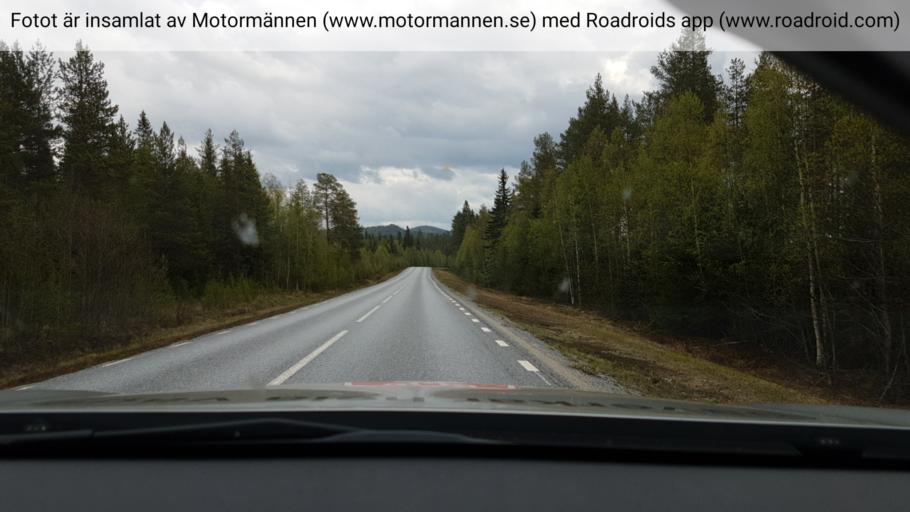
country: SE
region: Vaesterbotten
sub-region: Bjurholms Kommun
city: Bjurholm
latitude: 64.0250
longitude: 18.6538
